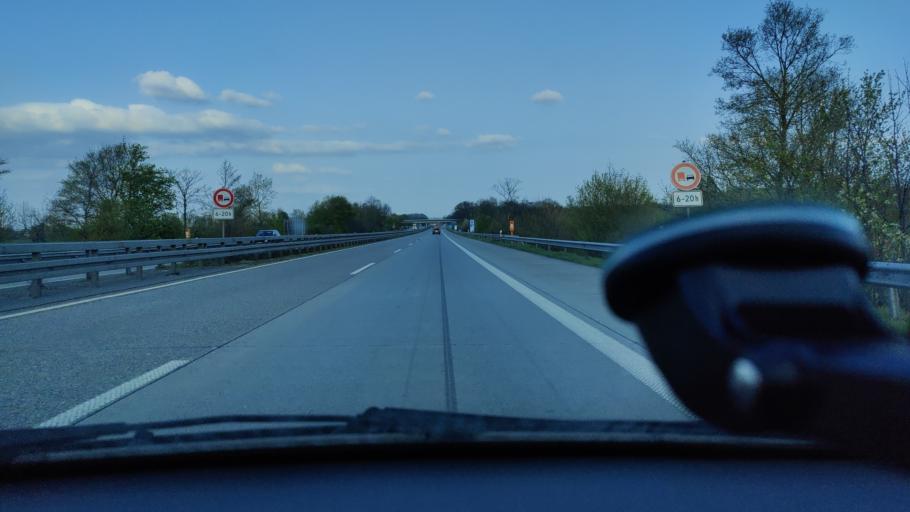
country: DE
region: North Rhine-Westphalia
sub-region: Regierungsbezirk Dusseldorf
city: Wachtendonk
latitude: 51.3899
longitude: 6.2880
